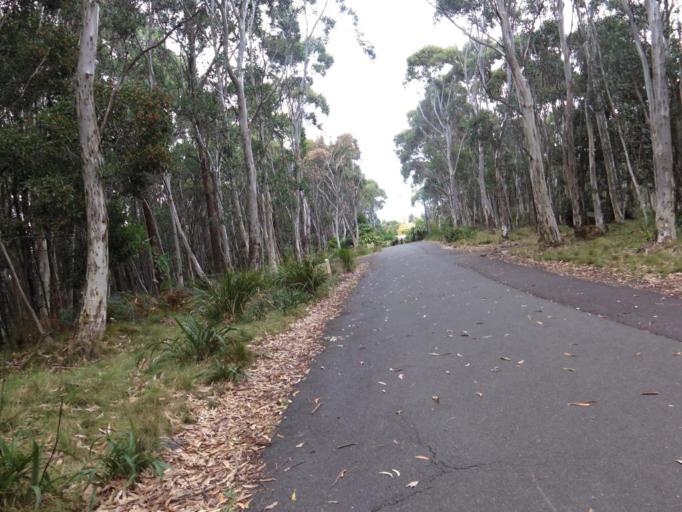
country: AU
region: Victoria
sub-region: Hume
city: Sunbury
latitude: -37.3883
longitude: 144.5765
